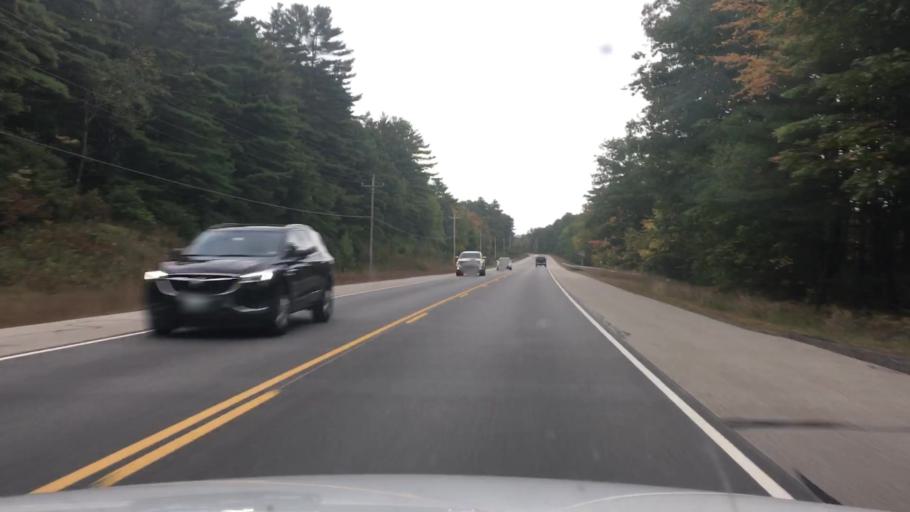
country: US
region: New Hampshire
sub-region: Strafford County
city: New Durham
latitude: 43.4466
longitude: -71.2024
